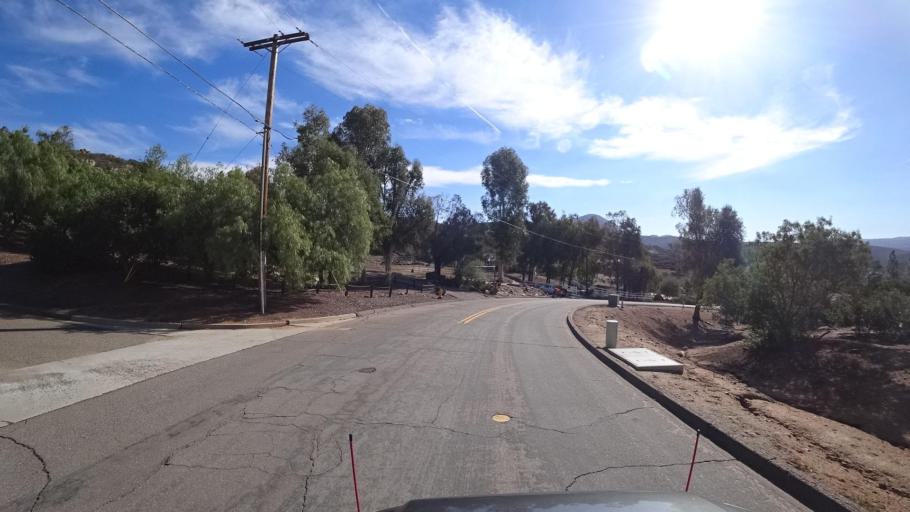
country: US
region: California
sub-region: San Diego County
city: Alpine
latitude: 32.8221
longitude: -116.7429
